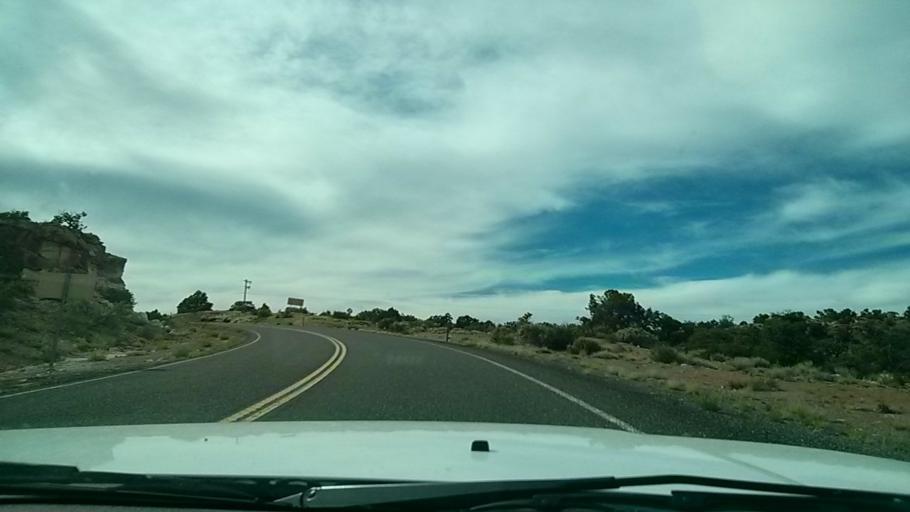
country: US
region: Utah
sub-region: Wayne County
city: Loa
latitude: 37.7497
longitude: -111.4566
